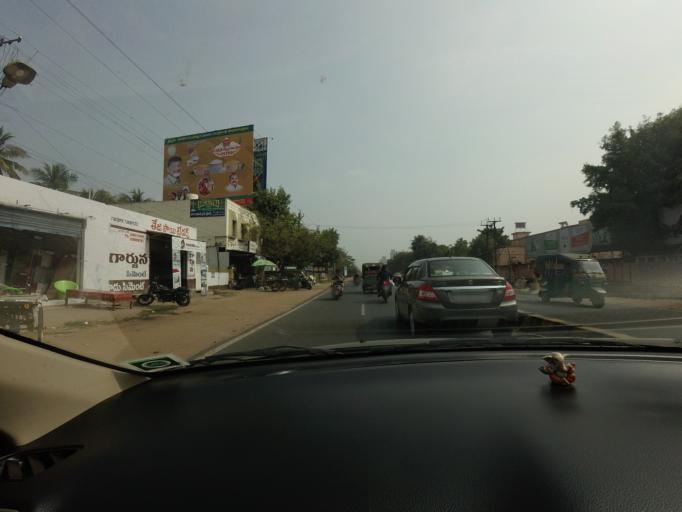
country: IN
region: Andhra Pradesh
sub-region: Krishna
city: Yanamalakuduru
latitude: 16.4896
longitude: 80.6730
